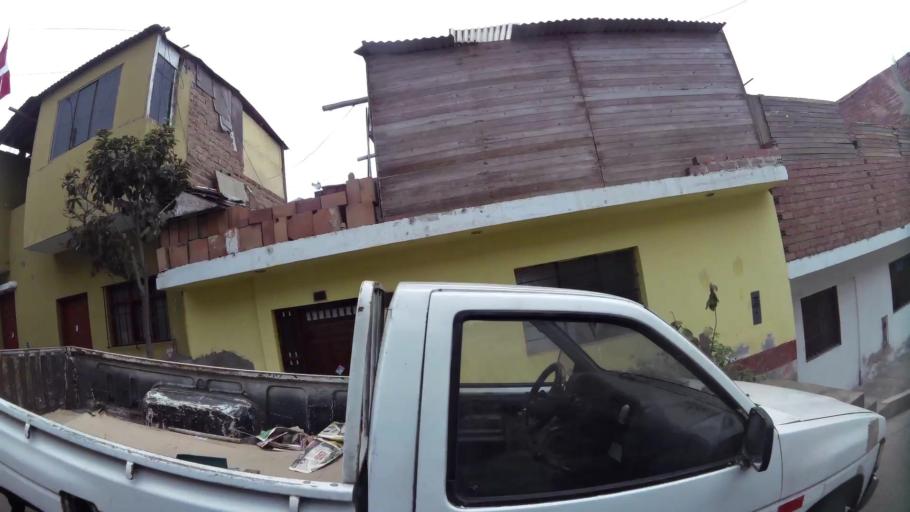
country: PE
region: Lima
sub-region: Lima
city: Surco
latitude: -12.1877
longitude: -77.0148
